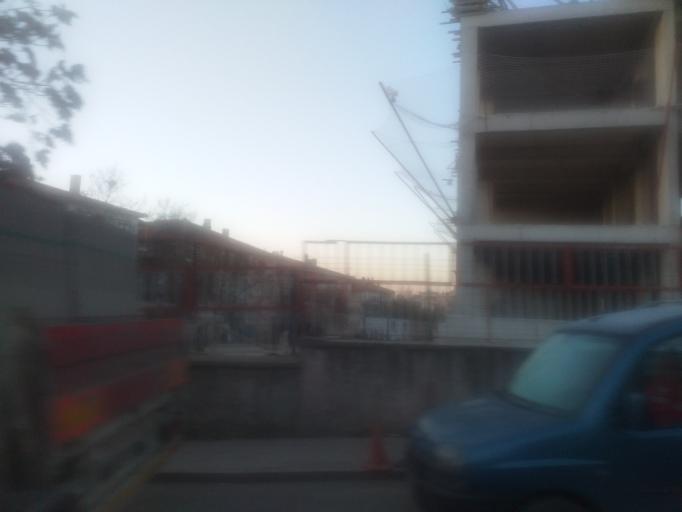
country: TR
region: Ankara
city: Ankara
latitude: 39.9785
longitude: 32.8381
